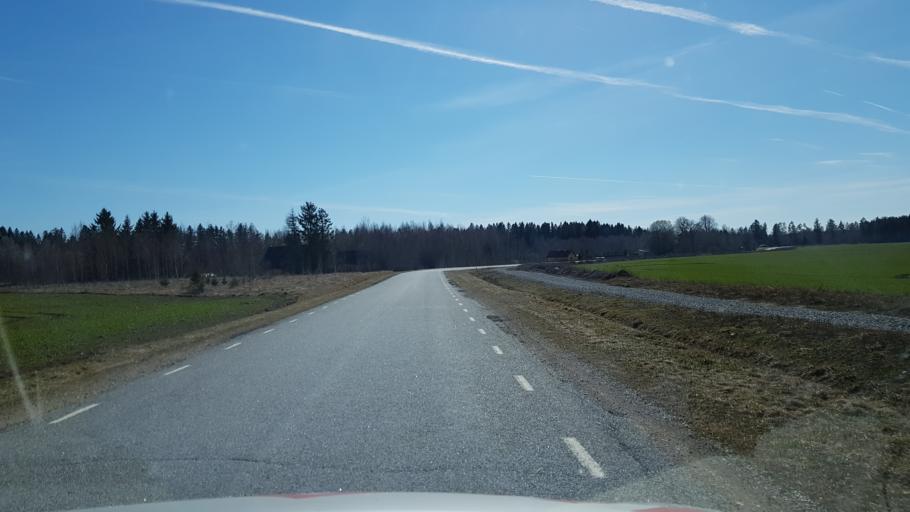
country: EE
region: Laeaene-Virumaa
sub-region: Viru-Nigula vald
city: Kunda
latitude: 59.3430
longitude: 26.6704
